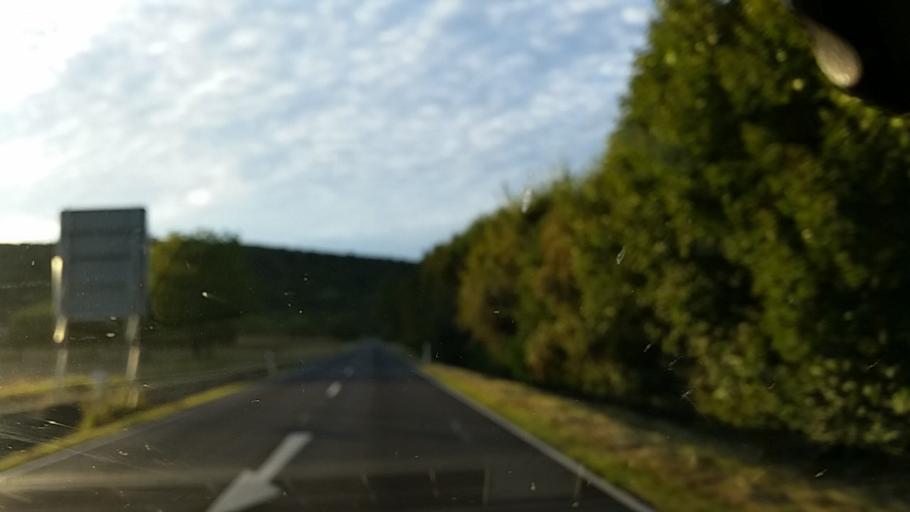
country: DE
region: Bavaria
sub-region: Regierungsbezirk Unterfranken
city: Zellingen
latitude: 49.9040
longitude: 9.8071
